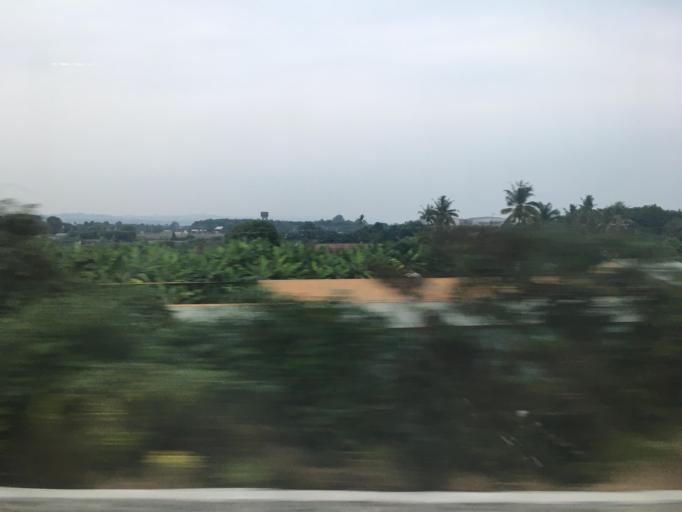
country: TW
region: Taiwan
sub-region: Pingtung
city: Pingtung
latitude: 22.6620
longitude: 120.4493
